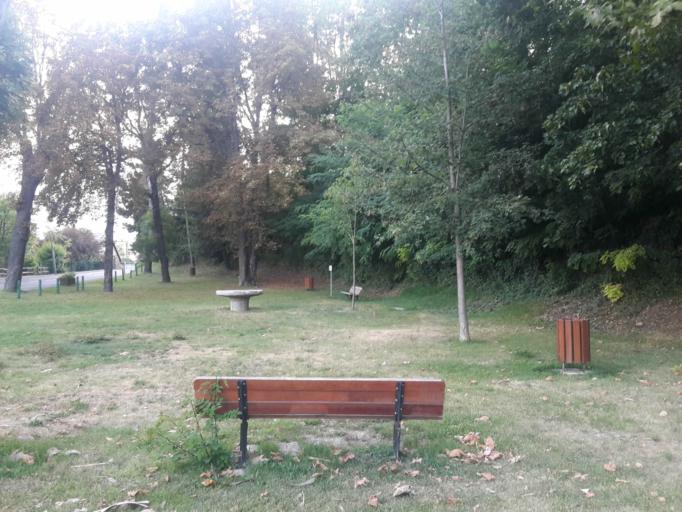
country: FR
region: Provence-Alpes-Cote d'Azur
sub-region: Departement des Hautes-Alpes
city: Embrun
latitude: 44.5618
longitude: 6.4896
